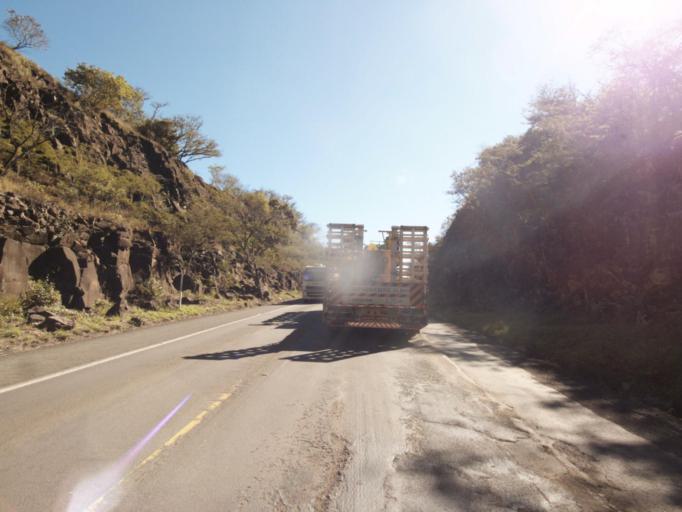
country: BR
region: Rio Grande do Sul
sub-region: Frederico Westphalen
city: Frederico Westphalen
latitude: -26.8132
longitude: -53.4358
